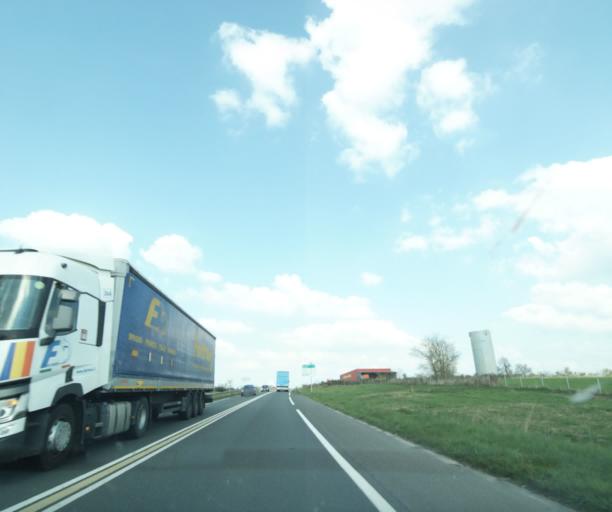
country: FR
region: Auvergne
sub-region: Departement de l'Allier
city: Montmarault
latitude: 46.3280
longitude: 2.9700
